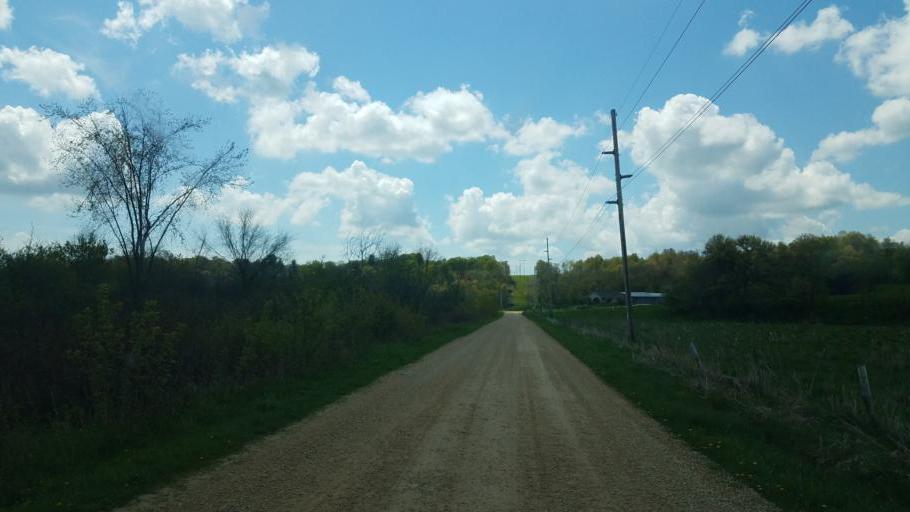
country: US
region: Wisconsin
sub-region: Vernon County
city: Hillsboro
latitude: 43.6804
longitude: -90.3325
